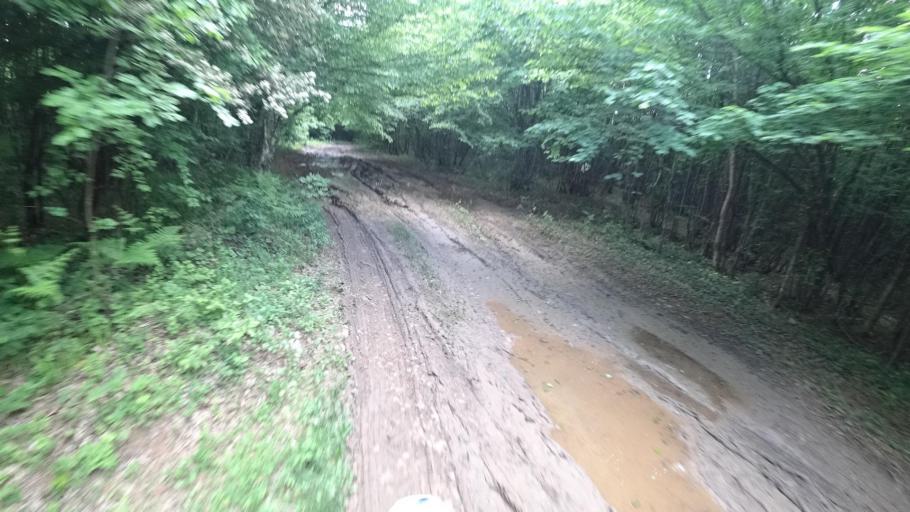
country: BA
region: Federation of Bosnia and Herzegovina
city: Bihac
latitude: 44.8110
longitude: 15.9269
